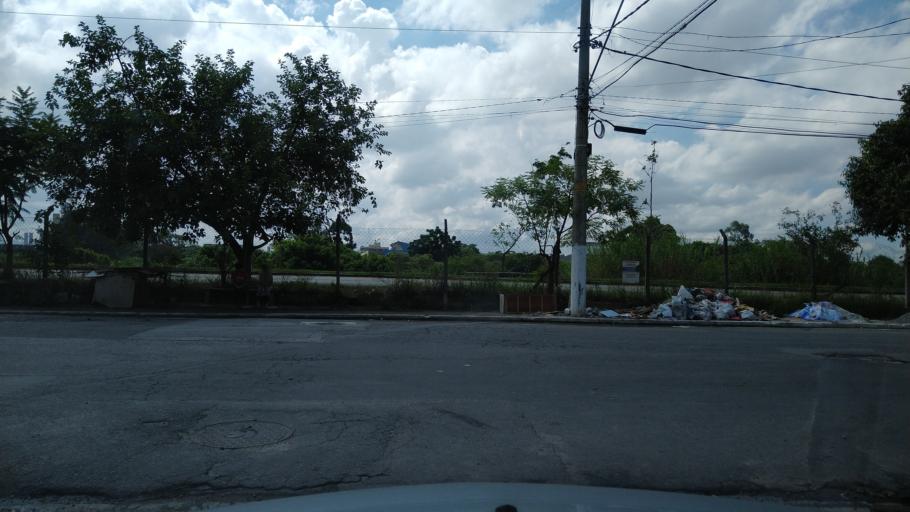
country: BR
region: Sao Paulo
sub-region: Guarulhos
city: Guarulhos
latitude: -23.4838
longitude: -46.4635
